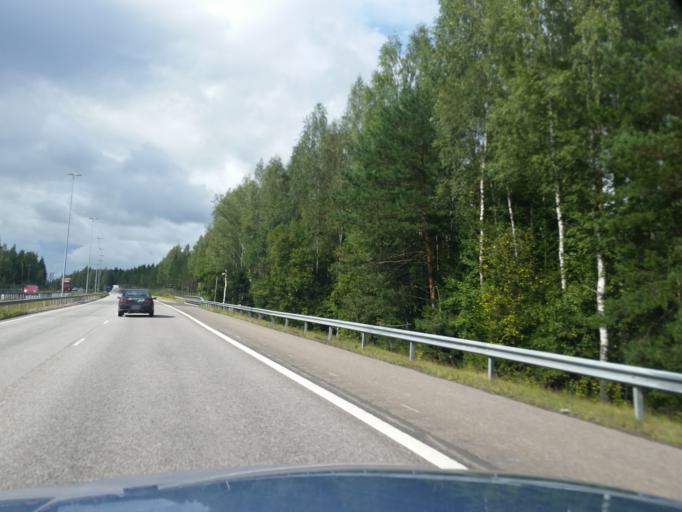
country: FI
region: Uusimaa
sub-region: Helsinki
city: Espoo
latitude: 60.2532
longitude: 24.5258
